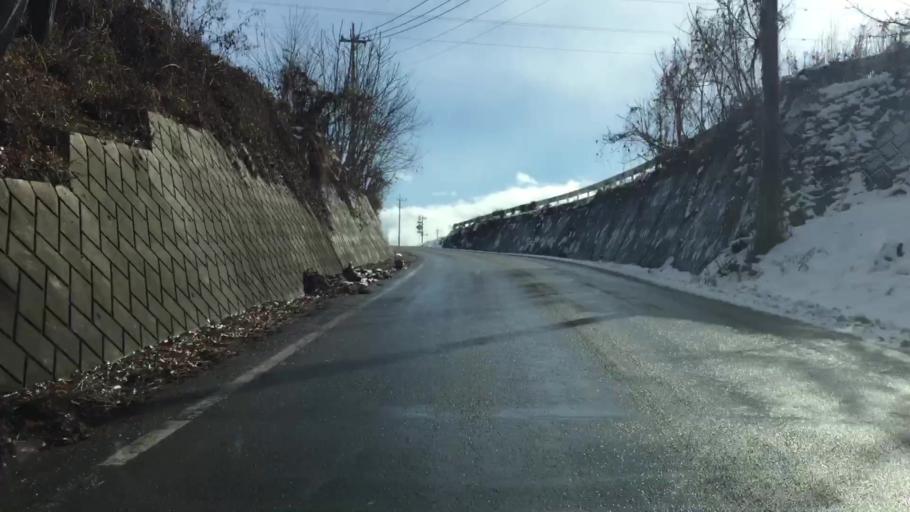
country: JP
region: Gunma
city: Numata
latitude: 36.6382
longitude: 139.0802
